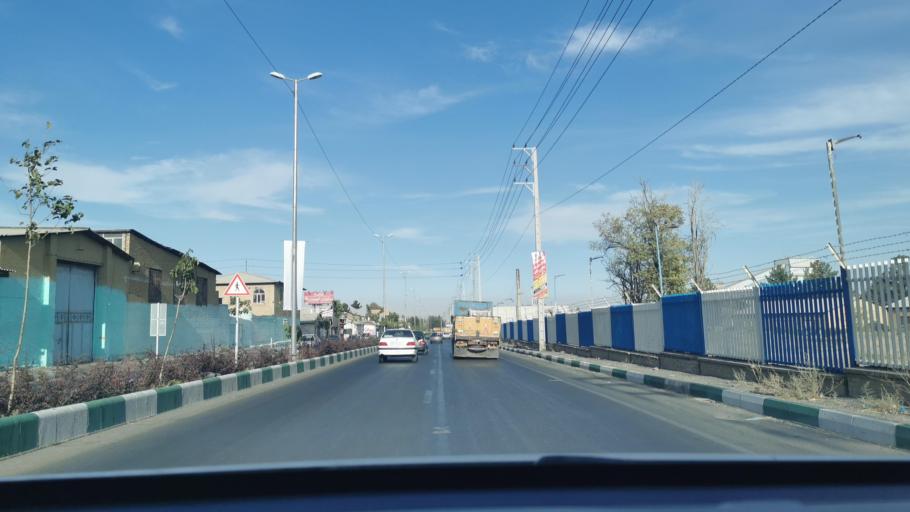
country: IR
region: Razavi Khorasan
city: Torqabeh
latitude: 36.4369
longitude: 59.4374
